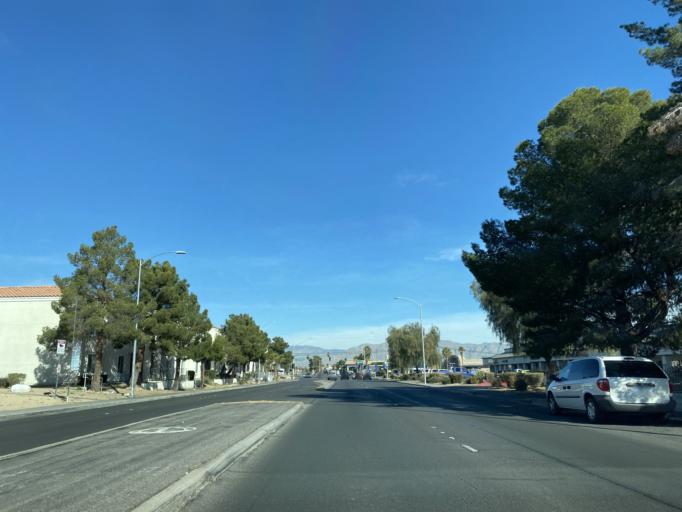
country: US
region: Nevada
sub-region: Clark County
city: Las Vegas
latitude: 36.2016
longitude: -115.2237
